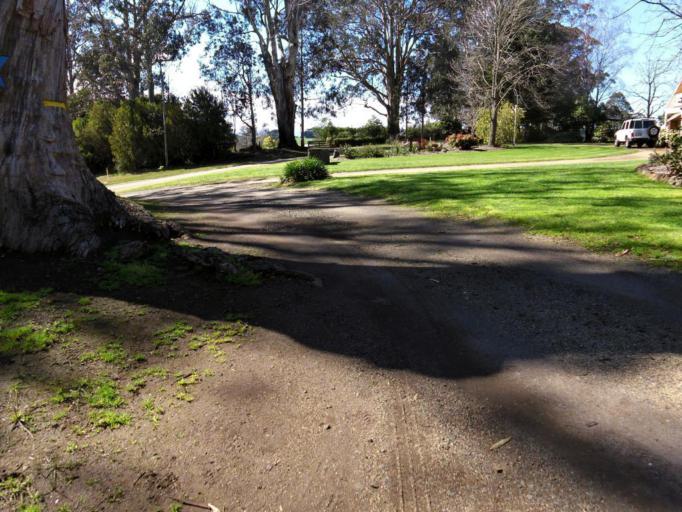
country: AU
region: Victoria
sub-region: Baw Baw
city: Warragul
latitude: -38.0308
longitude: 145.9546
